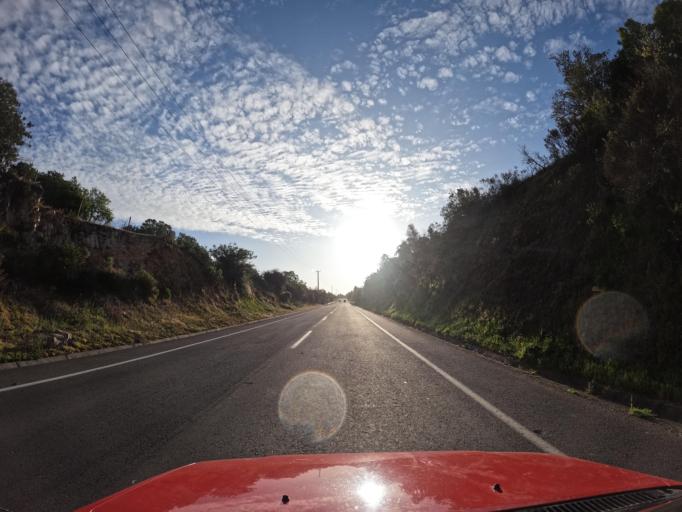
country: CL
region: Valparaiso
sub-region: San Antonio Province
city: San Antonio
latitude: -34.0491
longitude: -71.6111
